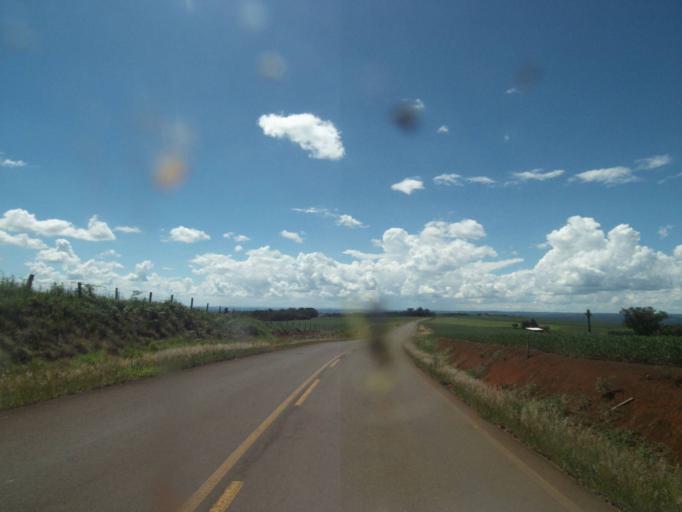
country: BR
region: Parana
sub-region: Pinhao
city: Pinhao
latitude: -25.8091
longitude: -52.0702
